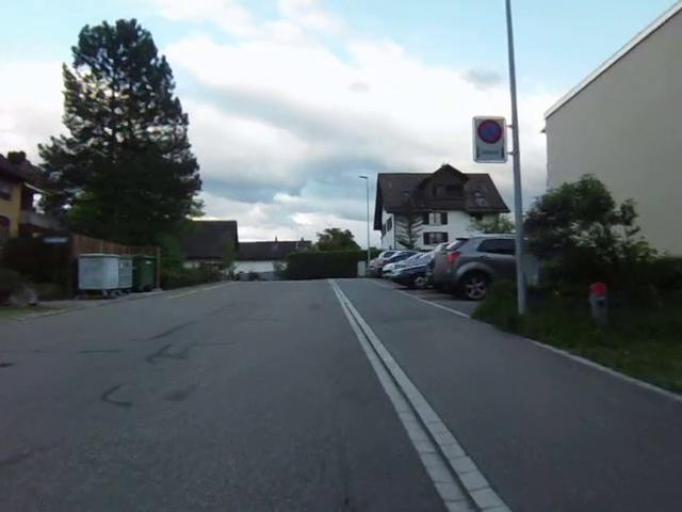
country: CH
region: Zurich
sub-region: Bezirk Hinwil
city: Rueti / Dorfzentrum, Suedl. Teil
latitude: 47.2505
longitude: 8.8585
